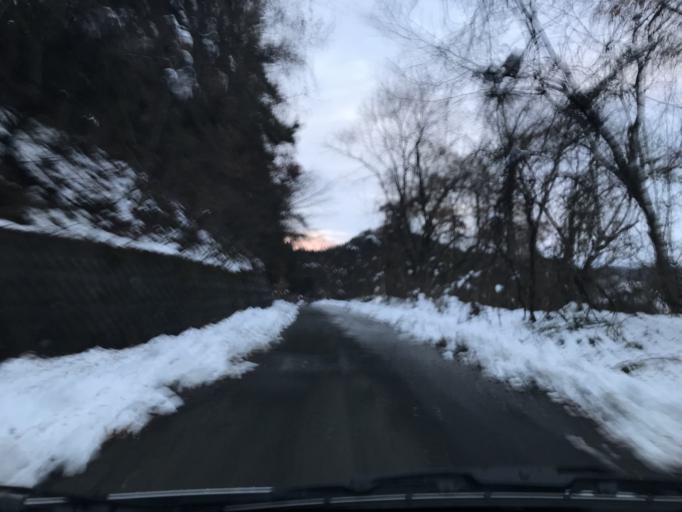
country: JP
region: Iwate
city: Mizusawa
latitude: 39.0501
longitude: 141.0221
